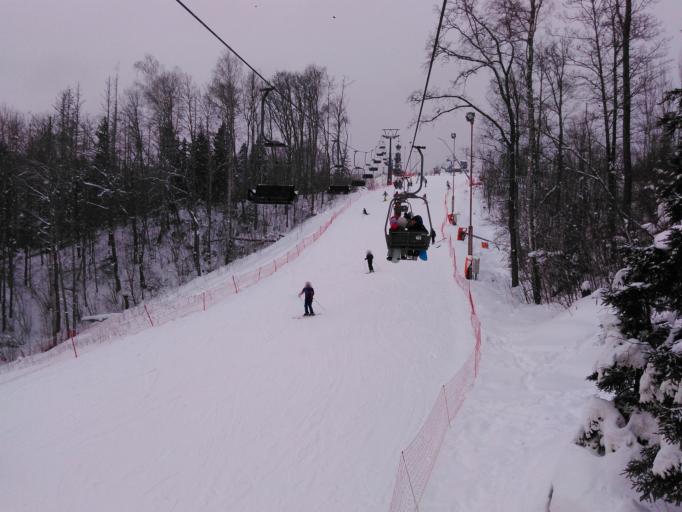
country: RU
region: Moskovskaya
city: Yakhroma
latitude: 56.2580
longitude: 37.4332
